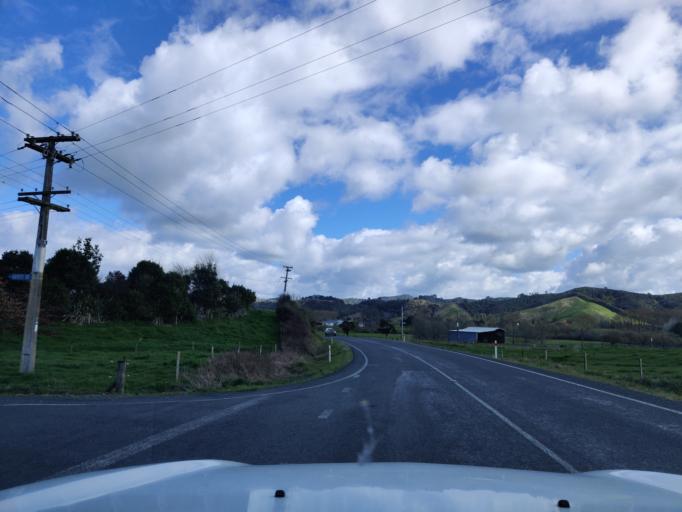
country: NZ
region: Waikato
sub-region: Waikato District
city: Ngaruawahia
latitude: -37.5774
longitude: 175.2300
